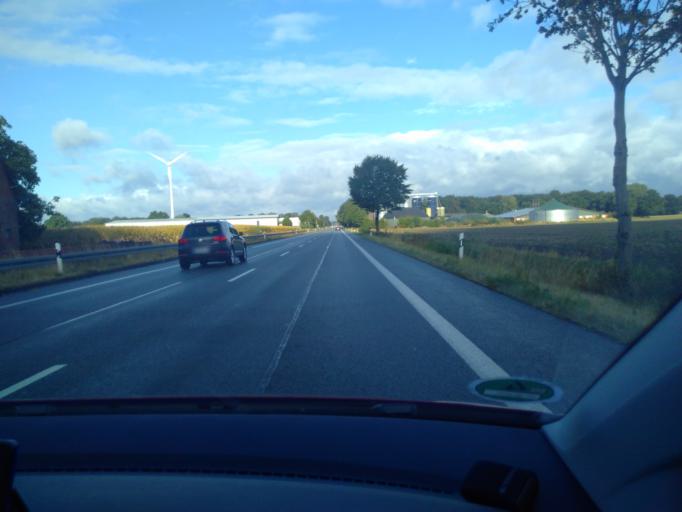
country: DE
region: North Rhine-Westphalia
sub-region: Regierungsbezirk Munster
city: Beelen
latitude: 51.9354
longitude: 8.0960
